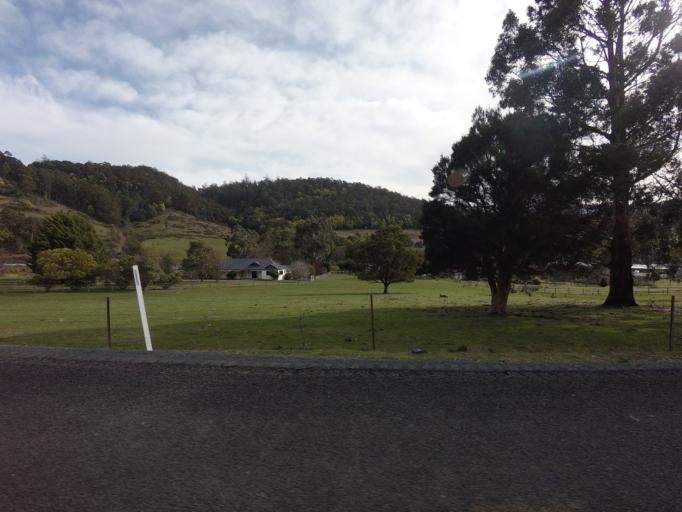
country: AU
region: Tasmania
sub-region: Kingborough
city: Margate
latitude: -42.9938
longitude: 147.1840
